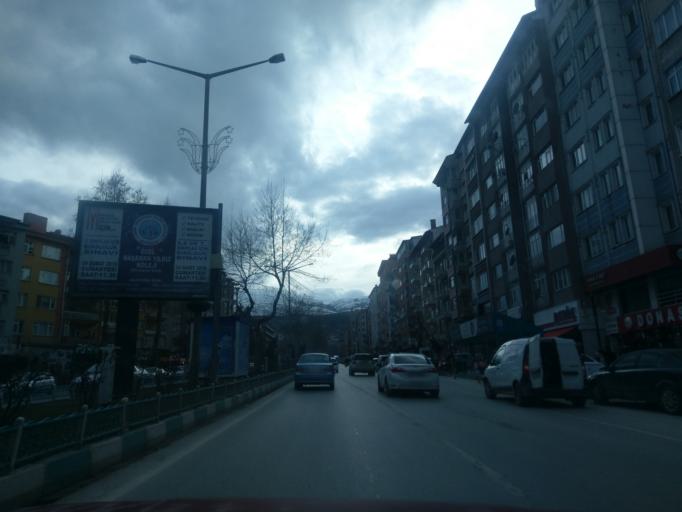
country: TR
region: Kuetahya
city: Kutahya
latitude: 39.4238
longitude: 29.9889
